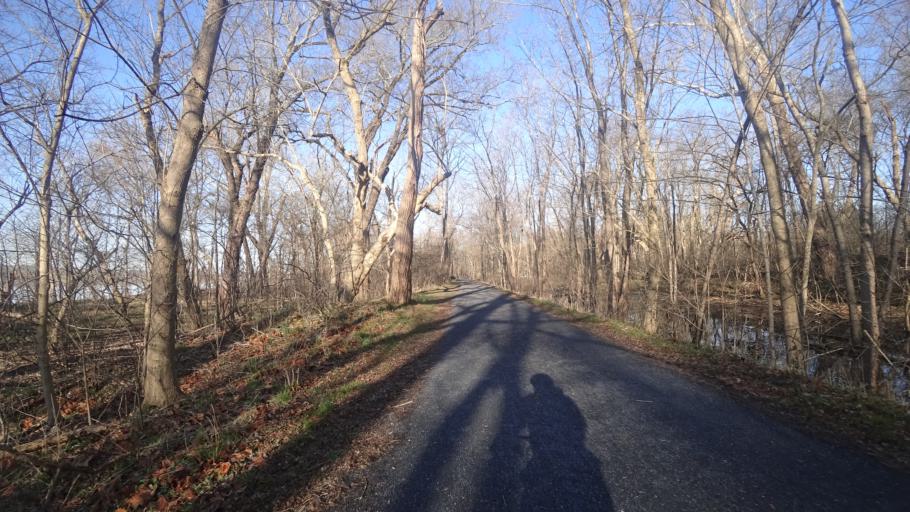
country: US
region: Virginia
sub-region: Loudoun County
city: Lowes Island
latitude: 39.0687
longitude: -77.3378
